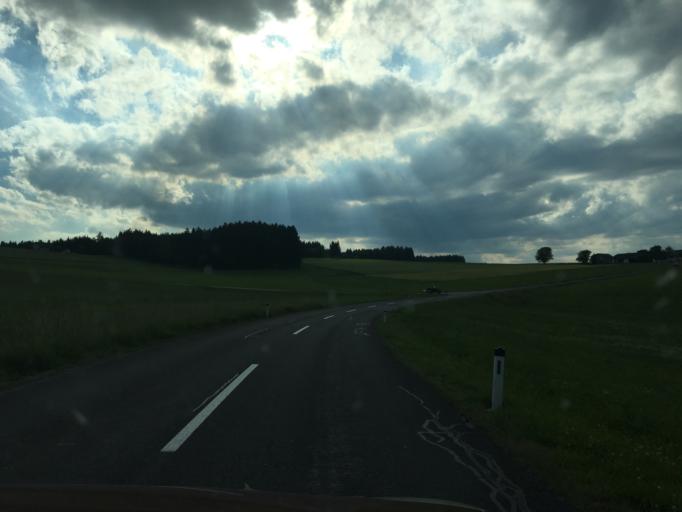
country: AT
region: Upper Austria
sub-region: Politischer Bezirk Urfahr-Umgebung
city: Reichenau im Muhlkreis
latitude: 48.4740
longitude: 14.3384
